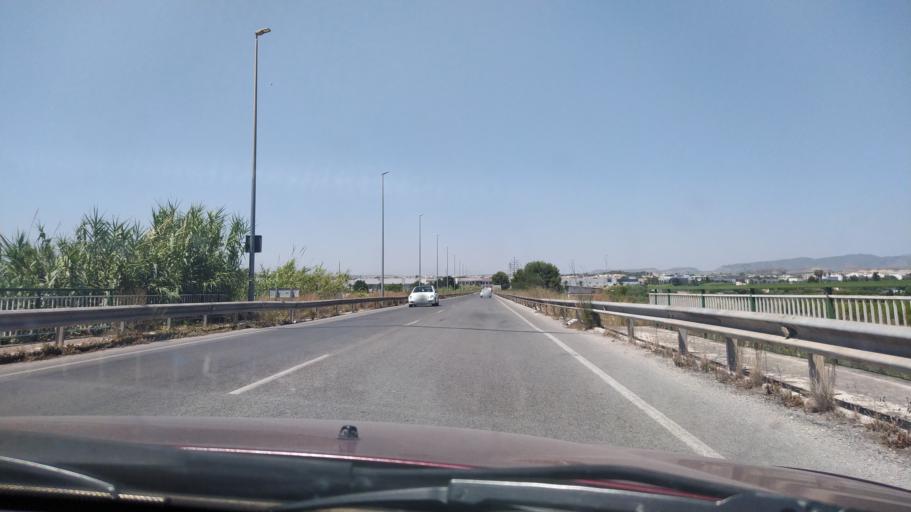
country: ES
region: Murcia
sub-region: Murcia
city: Lorqui
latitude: 38.0853
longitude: -1.2582
